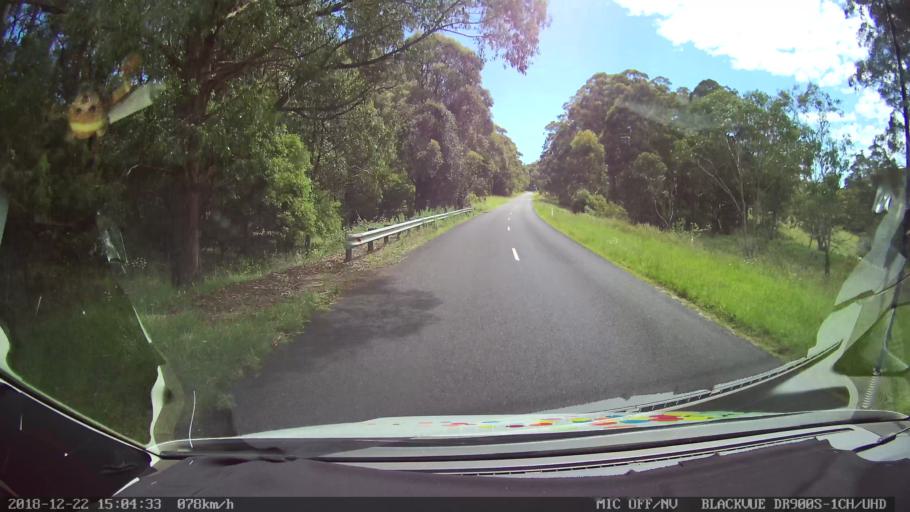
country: AU
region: New South Wales
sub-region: Bellingen
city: Dorrigo
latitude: -30.2760
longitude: 152.4375
